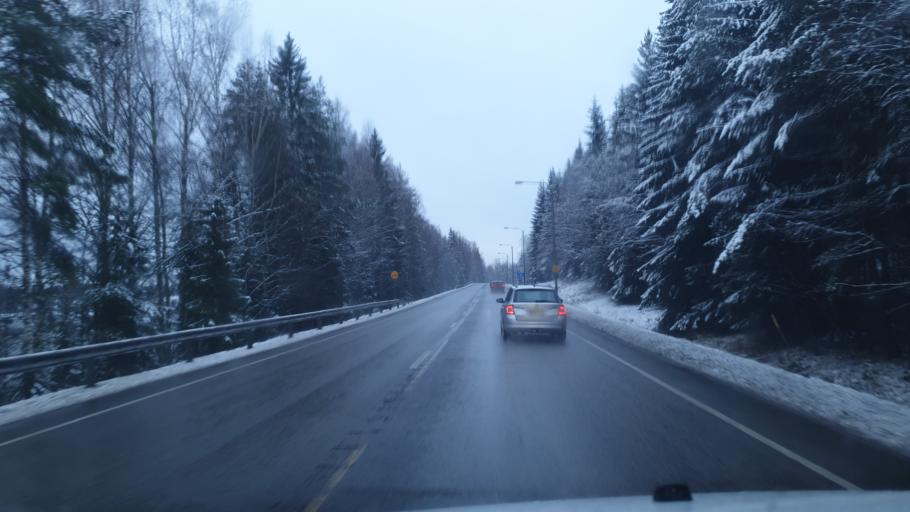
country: FI
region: Central Finland
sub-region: Jyvaeskylae
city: Jyvaeskylae
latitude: 62.3151
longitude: 25.7113
